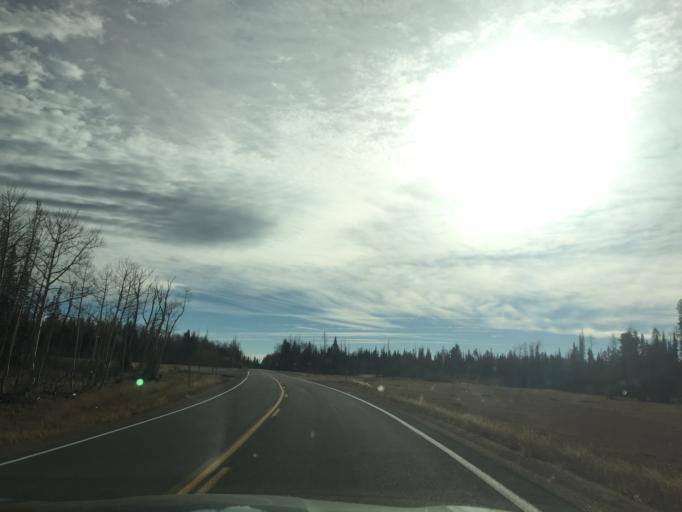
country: US
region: Utah
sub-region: Iron County
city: Parowan
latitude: 37.5417
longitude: -112.7832
